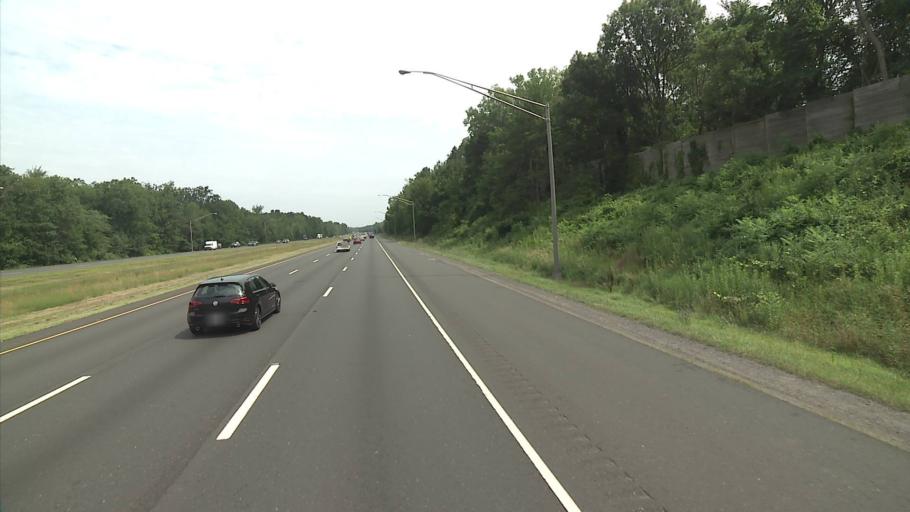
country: US
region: Connecticut
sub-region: Hartford County
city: Farmington
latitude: 41.6904
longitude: -72.8131
